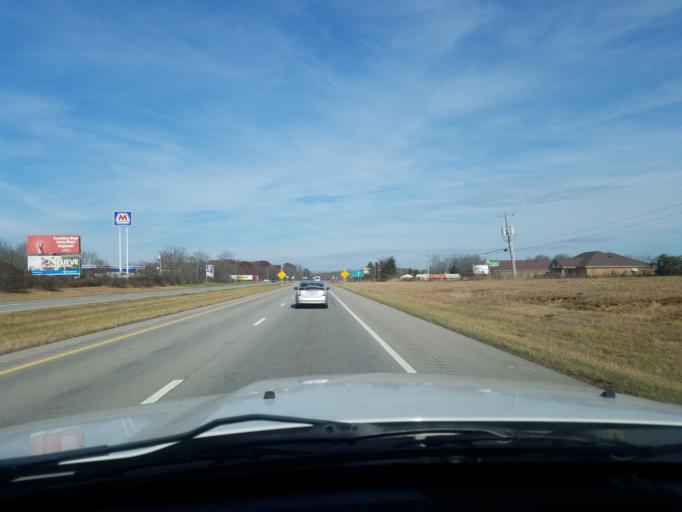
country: US
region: Ohio
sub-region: Athens County
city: Athens
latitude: 39.2330
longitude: -82.1956
